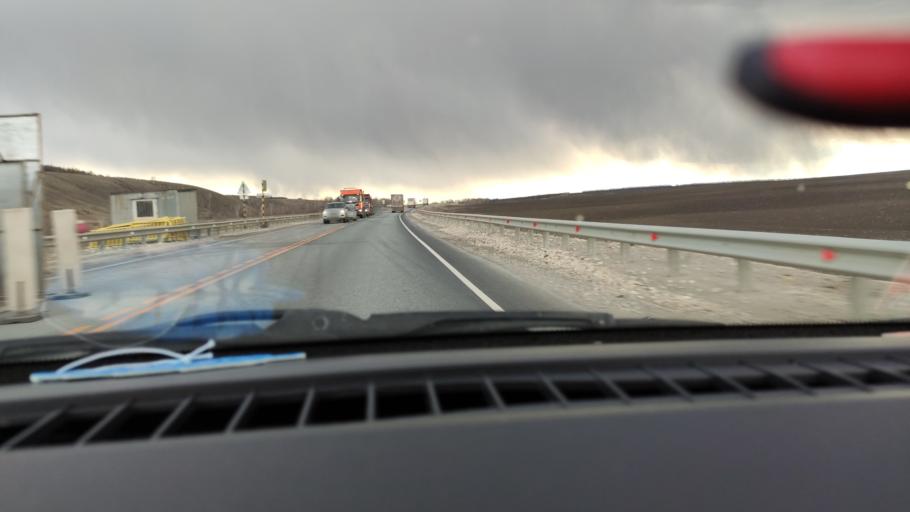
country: RU
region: Saratov
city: Yelshanka
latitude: 51.8621
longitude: 46.4996
